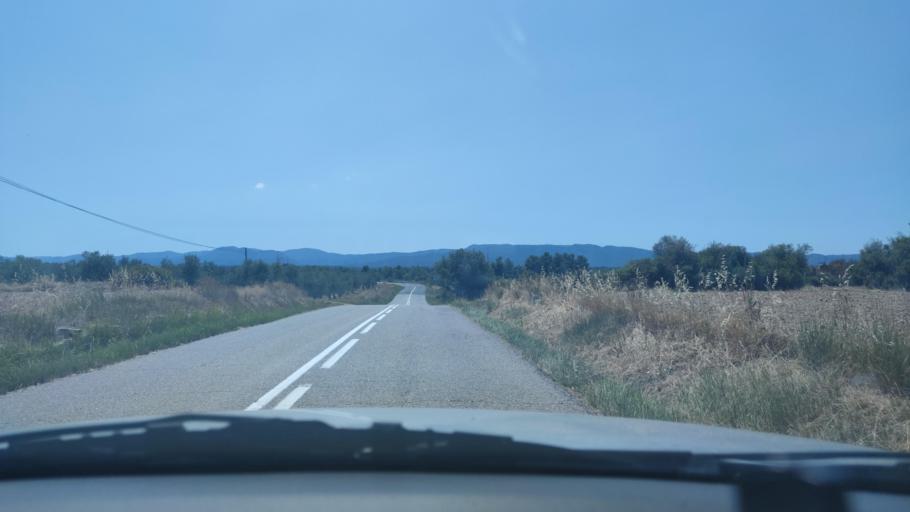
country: ES
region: Catalonia
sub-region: Provincia de Lleida
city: Vinaixa
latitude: 41.4192
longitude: 0.9545
